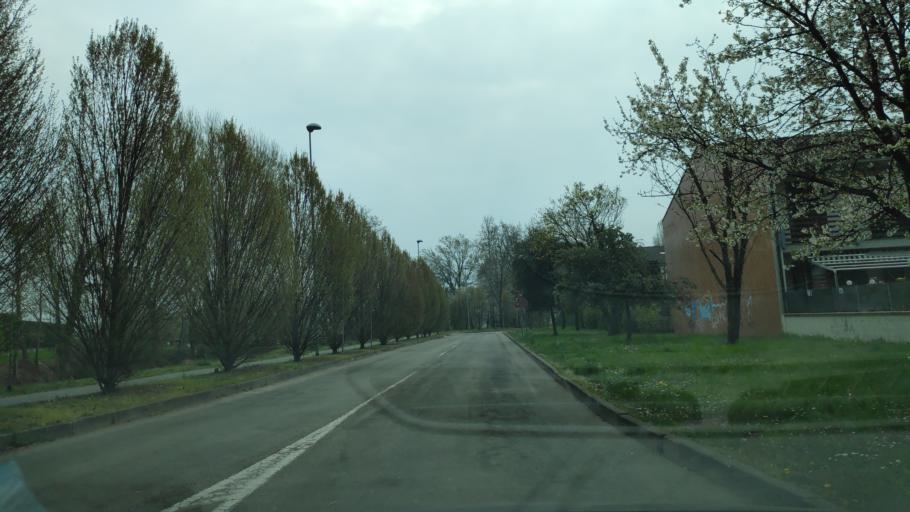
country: IT
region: Lombardy
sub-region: Citta metropolitana di Milano
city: Liscate
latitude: 45.4789
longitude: 9.4159
